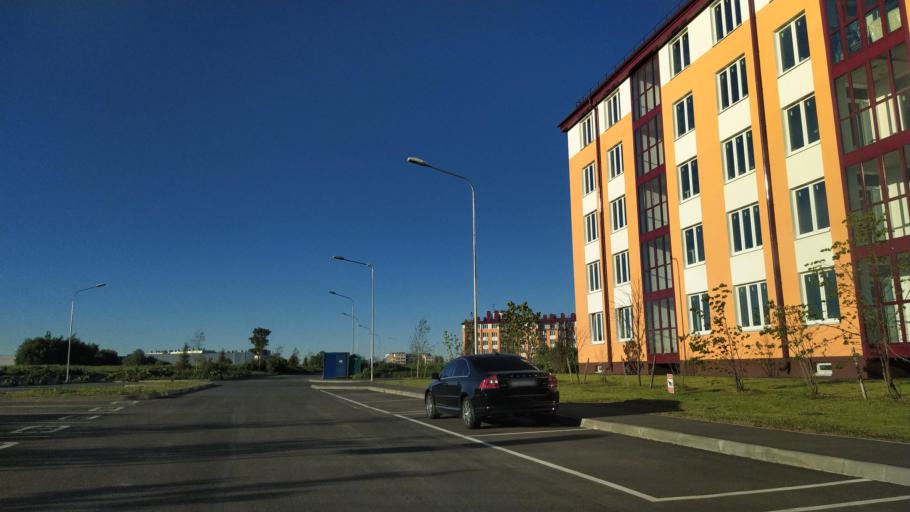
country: RU
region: St.-Petersburg
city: Aleksandrovskaya
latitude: 59.7544
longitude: 30.3580
